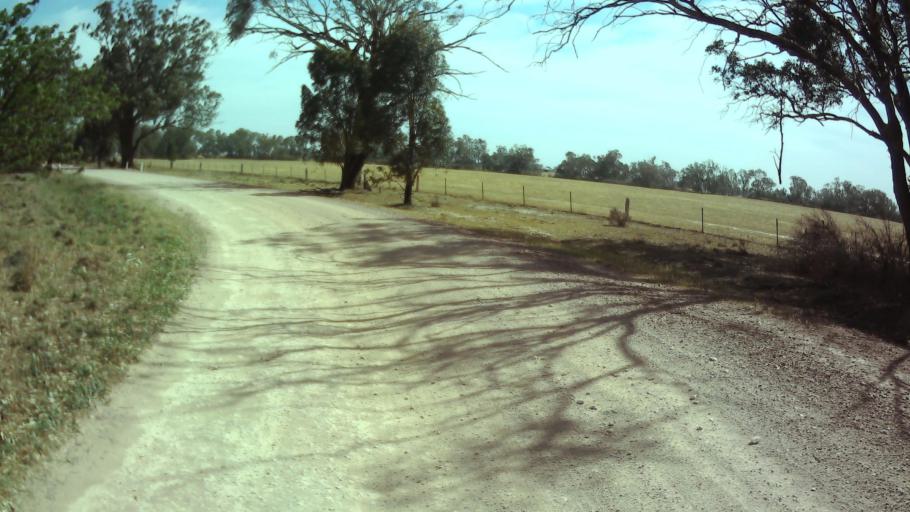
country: AU
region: New South Wales
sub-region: Weddin
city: Grenfell
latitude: -34.0370
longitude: 148.0813
